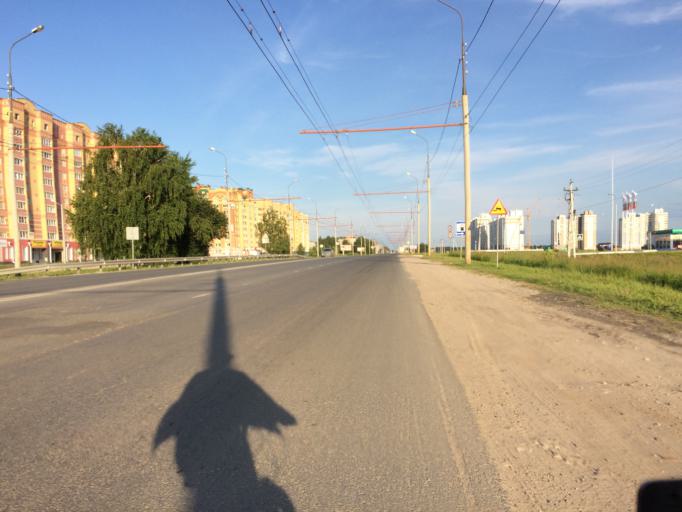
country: RU
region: Mariy-El
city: Medvedevo
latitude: 56.6397
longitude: 47.8157
